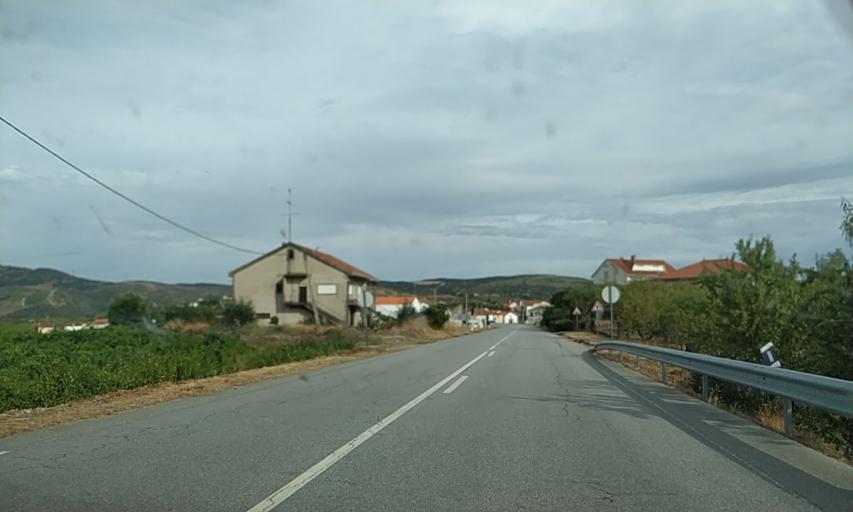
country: PT
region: Viseu
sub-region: Sao Joao da Pesqueira
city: Sao Joao da Pesqueira
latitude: 41.0996
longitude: -7.3816
